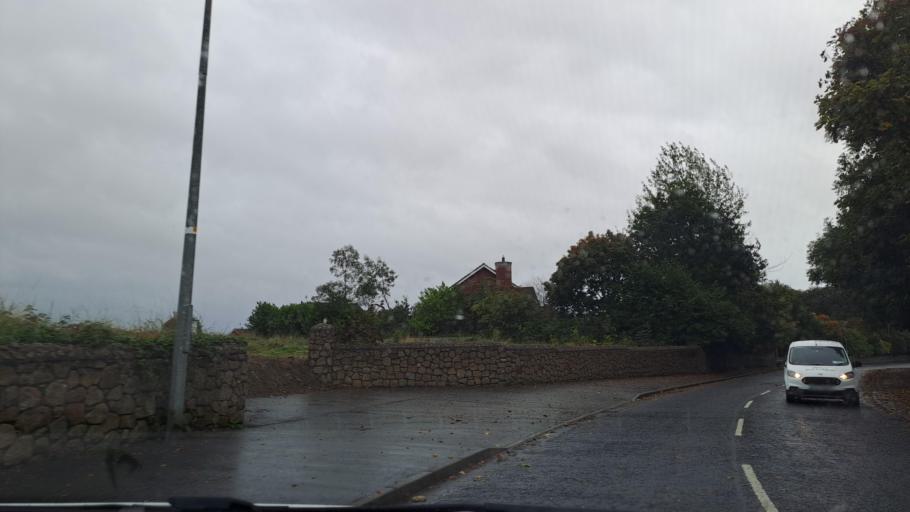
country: IE
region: Leinster
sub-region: Lu
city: Blackrock
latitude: 53.9619
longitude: -6.3770
